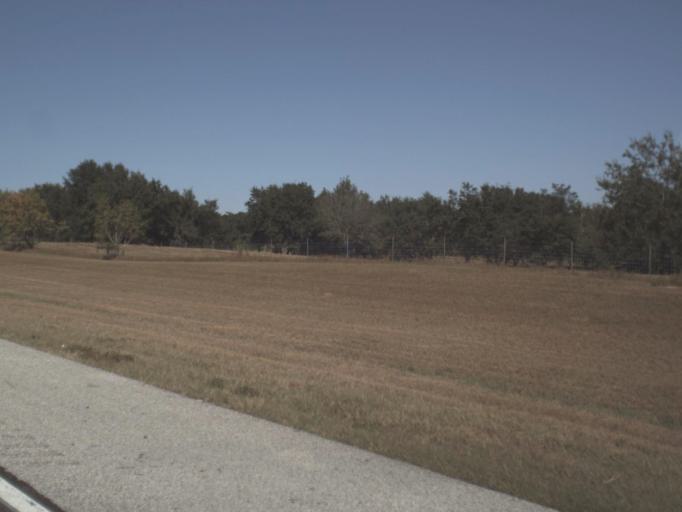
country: US
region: Florida
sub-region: Lake County
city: Minneola
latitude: 28.6118
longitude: -81.7313
